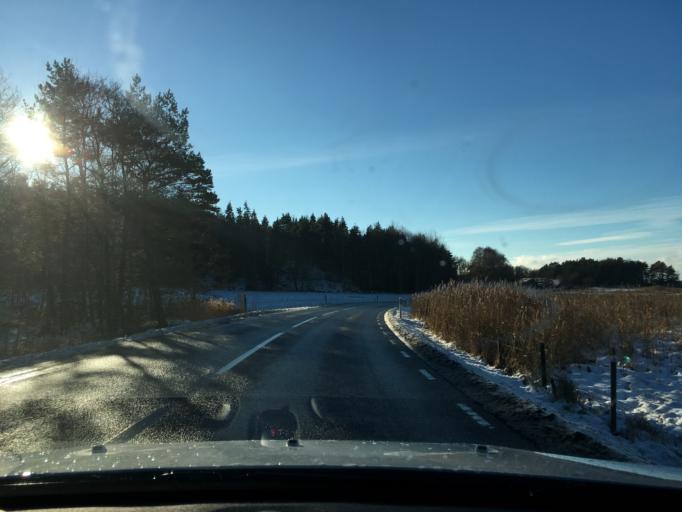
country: SE
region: Vaestra Goetaland
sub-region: Tjorns Kommun
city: Myggenas
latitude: 58.1134
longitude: 11.7030
